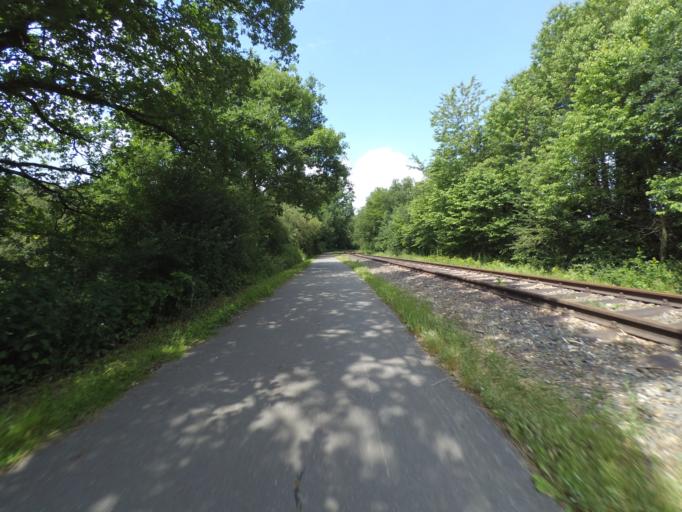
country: DE
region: North Rhine-Westphalia
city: Stolberg
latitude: 50.7155
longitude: 6.1960
